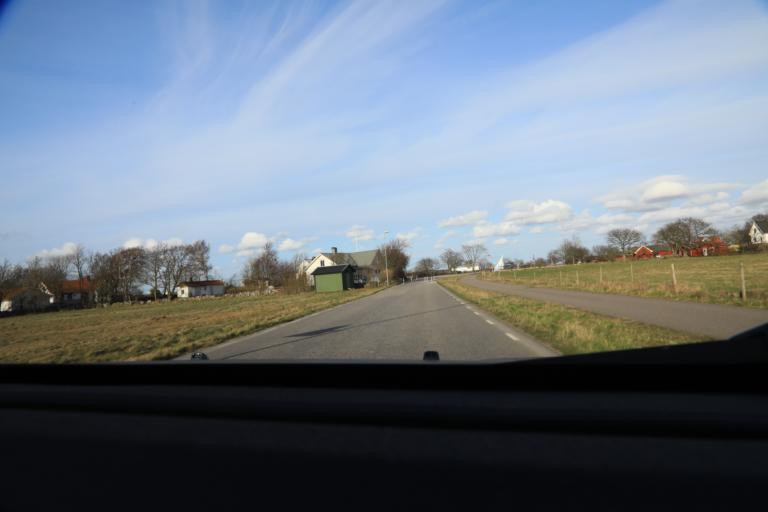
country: SE
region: Halland
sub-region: Varbergs Kommun
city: Varberg
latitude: 57.1206
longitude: 12.2189
